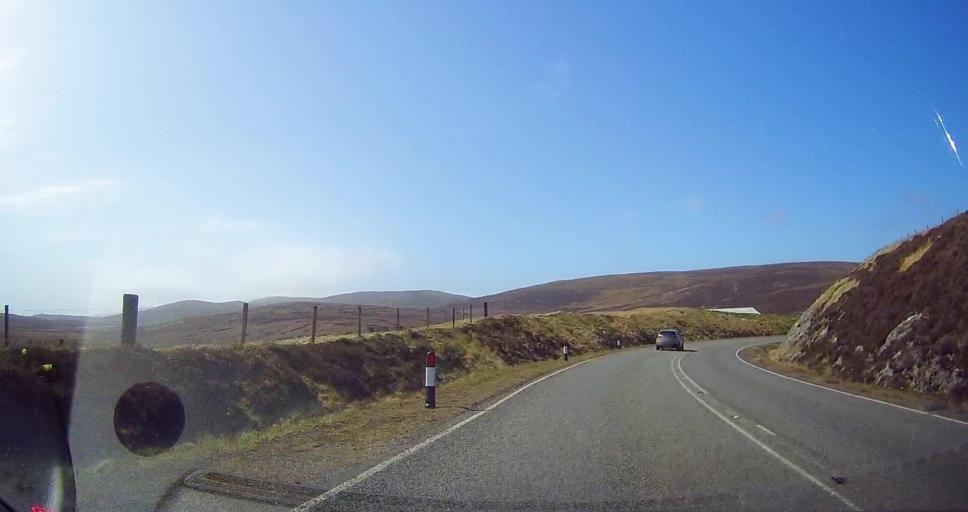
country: GB
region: Scotland
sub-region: Shetland Islands
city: Lerwick
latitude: 60.1381
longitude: -1.2267
